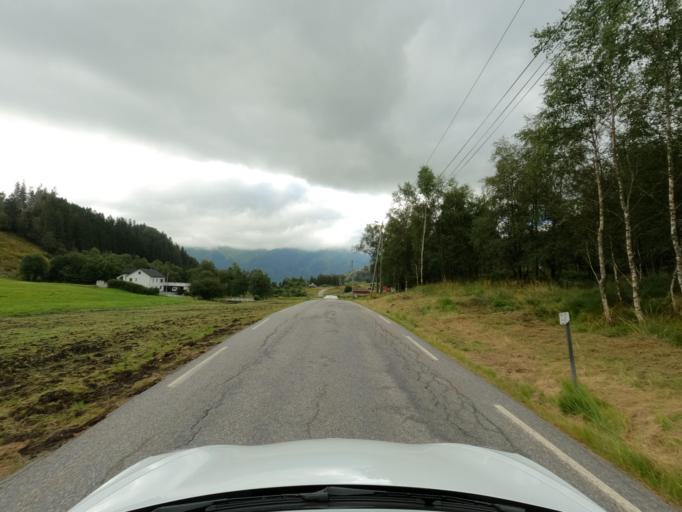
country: NO
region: Hordaland
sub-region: Bergen
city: Espeland
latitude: 60.3872
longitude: 5.4381
